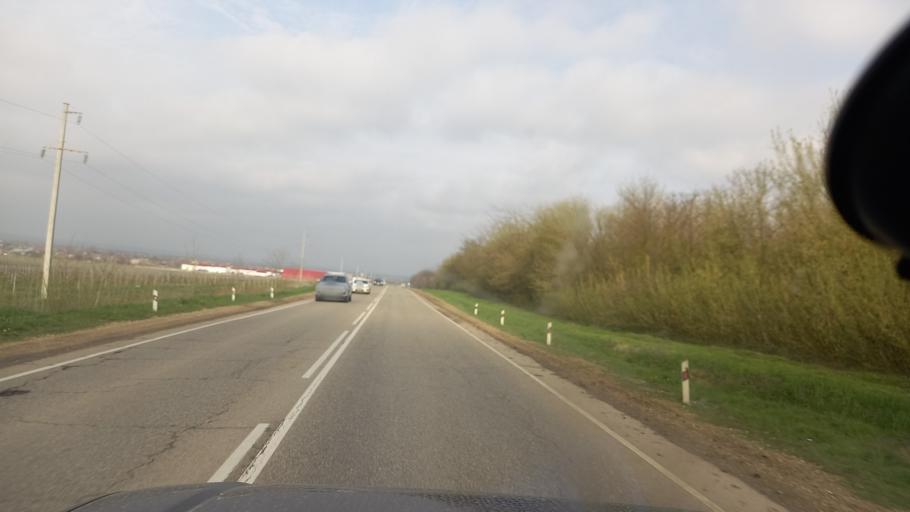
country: RU
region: Krasnodarskiy
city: Varenikovskaya
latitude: 45.1073
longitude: 37.6227
